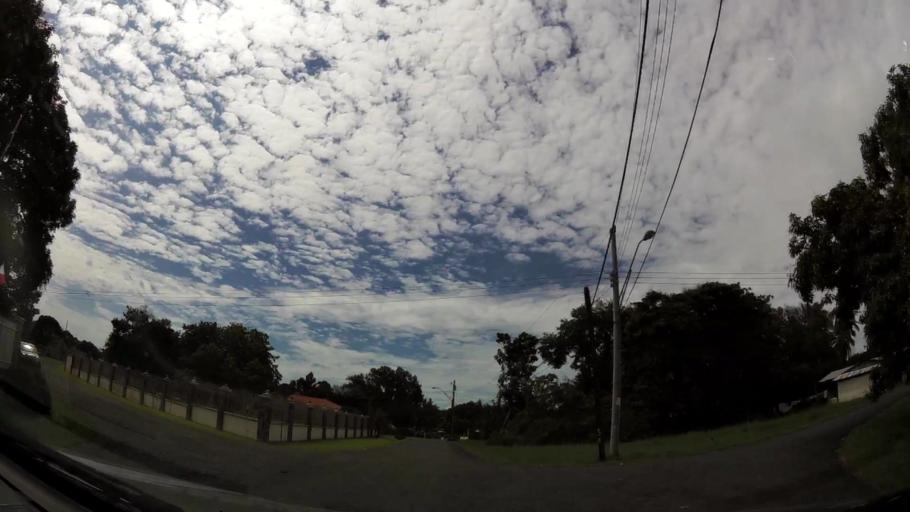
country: PA
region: Panama
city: Nueva Gorgona
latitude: 8.5354
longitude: -79.9205
